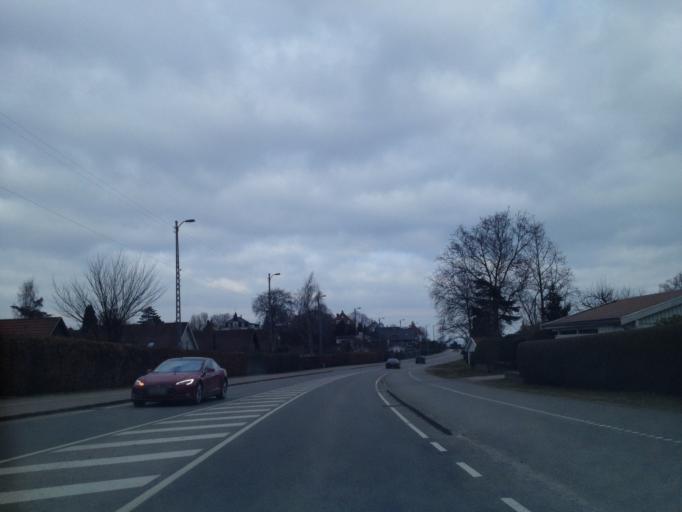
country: DK
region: Capital Region
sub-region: Helsingor Kommune
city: Espergaerde
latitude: 55.9859
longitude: 12.5514
